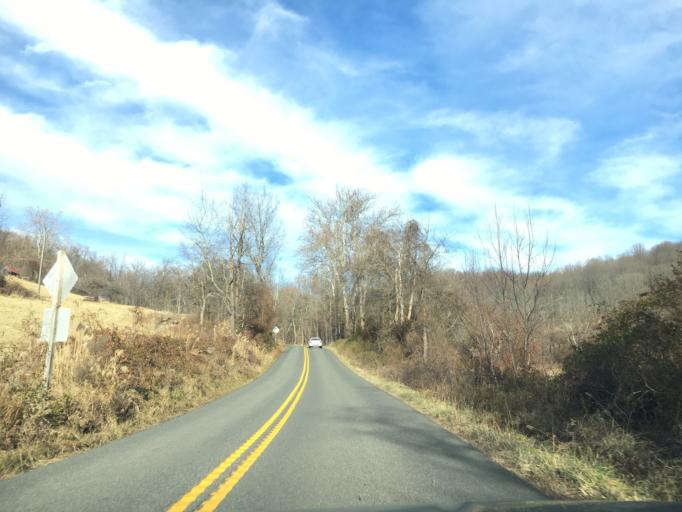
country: US
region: Virginia
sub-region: Warren County
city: Apple Mountain Lake
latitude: 38.8820
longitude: -78.0029
